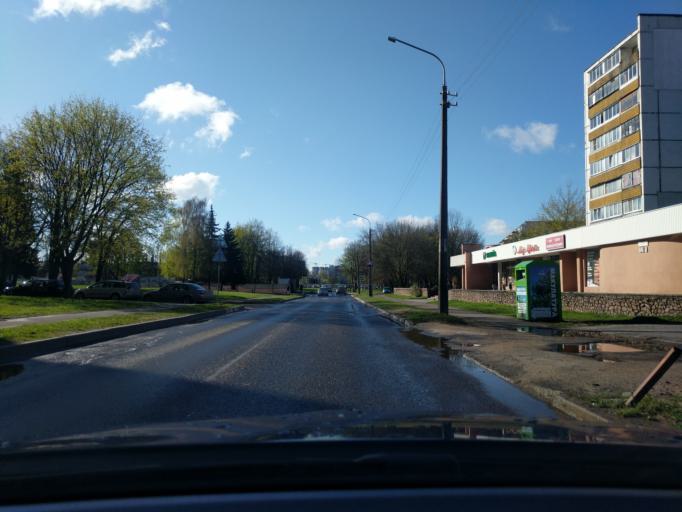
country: BY
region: Minsk
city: Novoye Medvezhino
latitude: 53.9006
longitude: 27.5058
